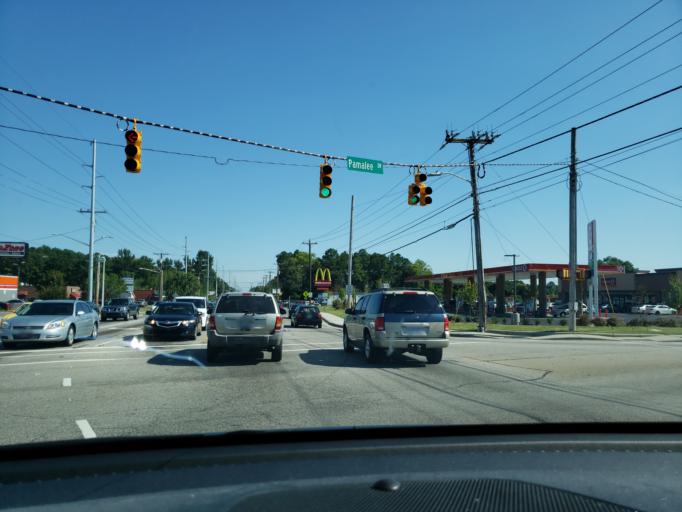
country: US
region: North Carolina
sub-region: Cumberland County
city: Fayetteville
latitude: 35.0971
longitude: -78.9157
